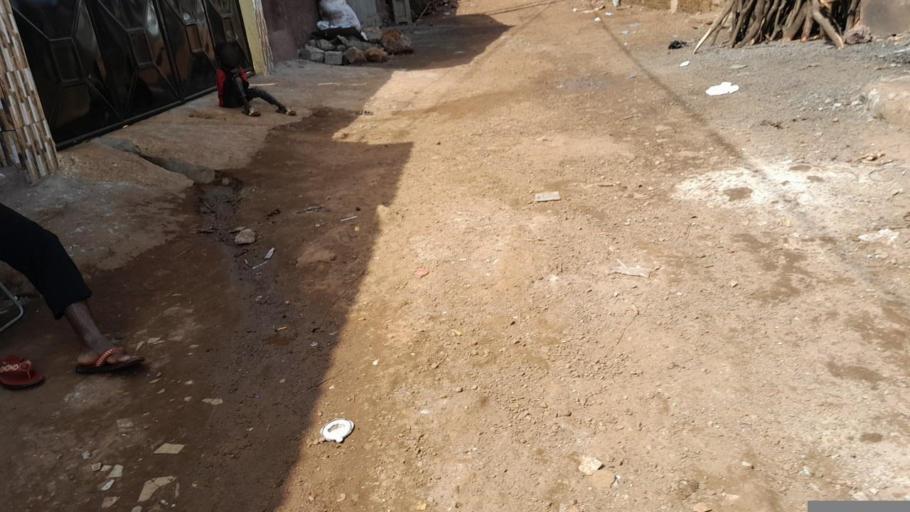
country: GN
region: Conakry
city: Conakry
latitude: 9.6113
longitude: -13.6152
